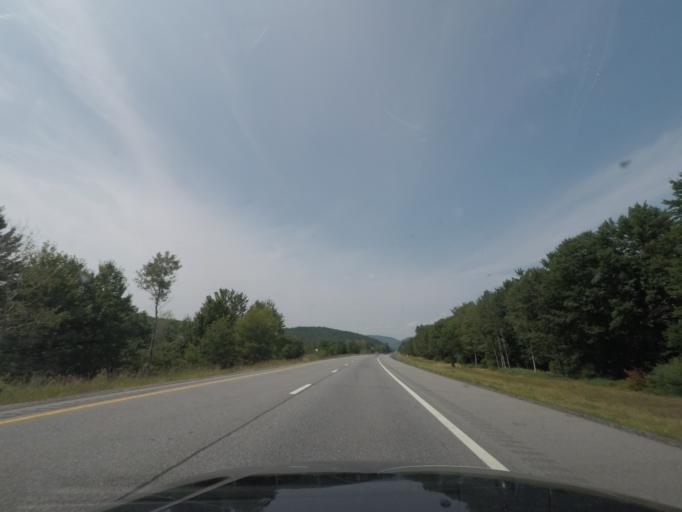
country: US
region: New York
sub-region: Warren County
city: Warrensburg
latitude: 43.6969
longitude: -73.8052
